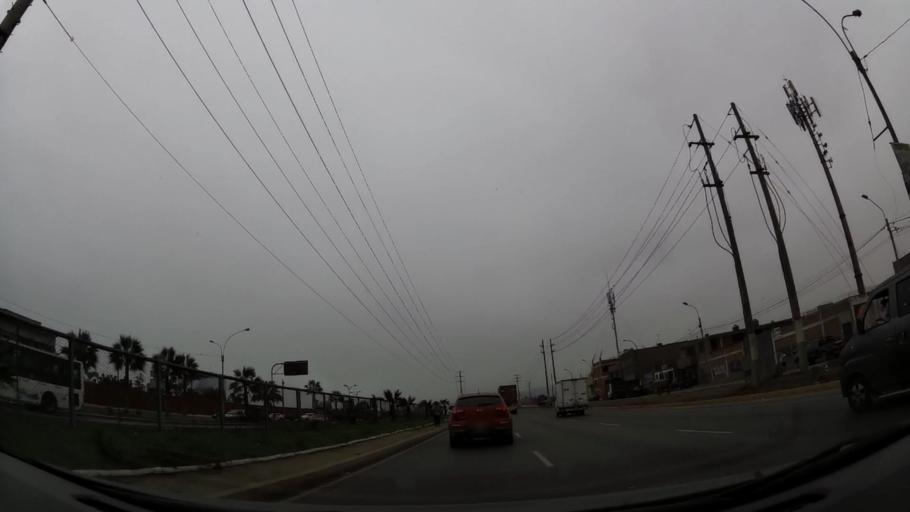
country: PE
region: Callao
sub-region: Callao
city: Callao
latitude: -11.9771
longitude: -77.1250
